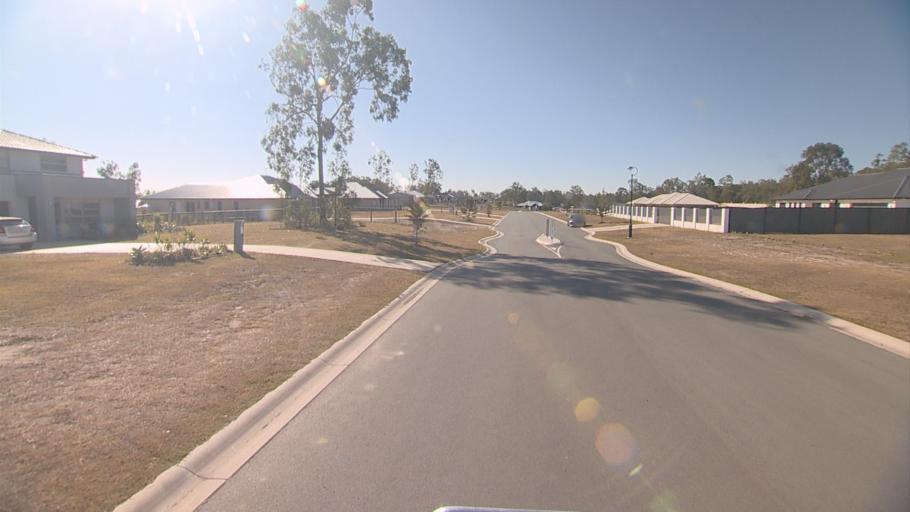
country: AU
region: Queensland
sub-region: Logan
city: Cedar Vale
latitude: -27.8701
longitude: 153.0480
